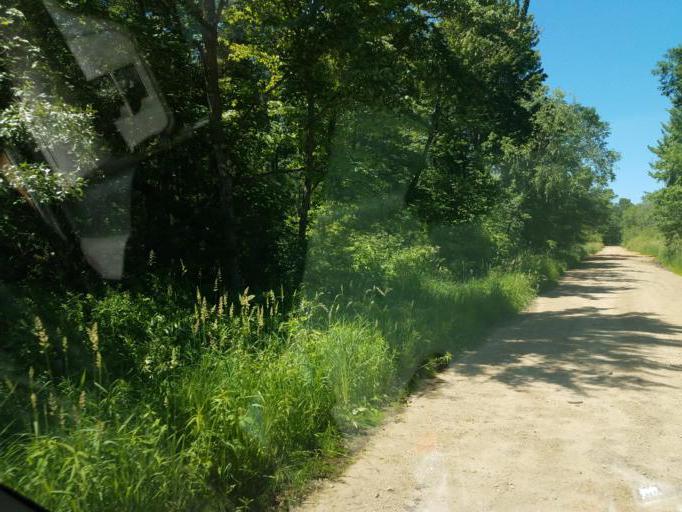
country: US
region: Wisconsin
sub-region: Adams County
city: Friendship
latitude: 44.0252
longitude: -89.9724
